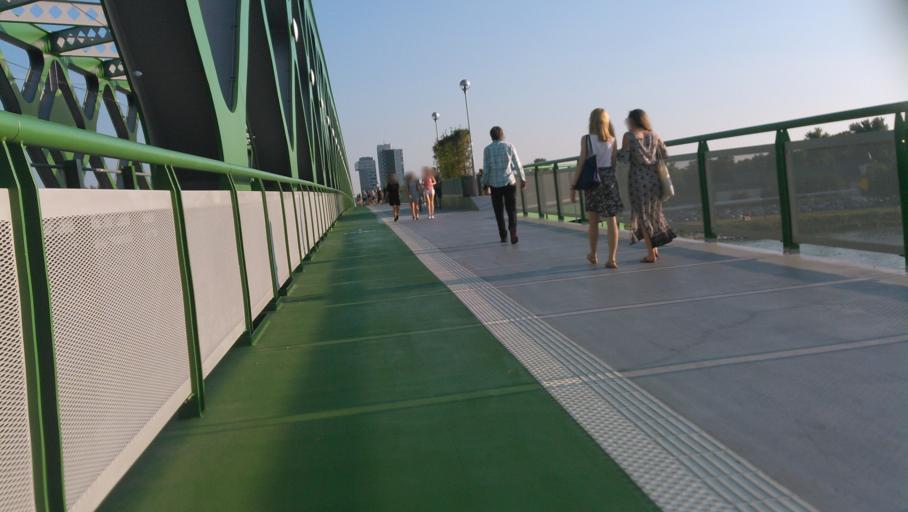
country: SK
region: Bratislavsky
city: Bratislava
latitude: 48.1392
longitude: 17.1171
